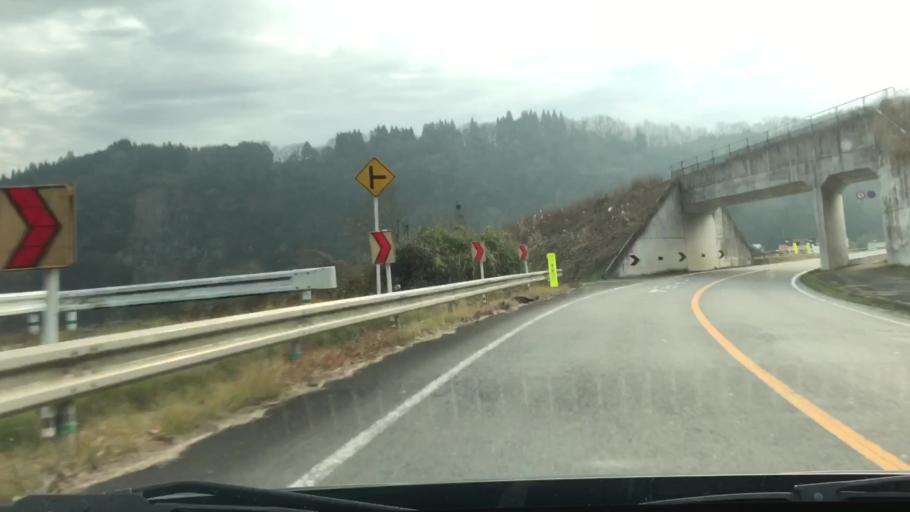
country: JP
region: Oita
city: Takedamachi
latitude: 32.9829
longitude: 131.5465
